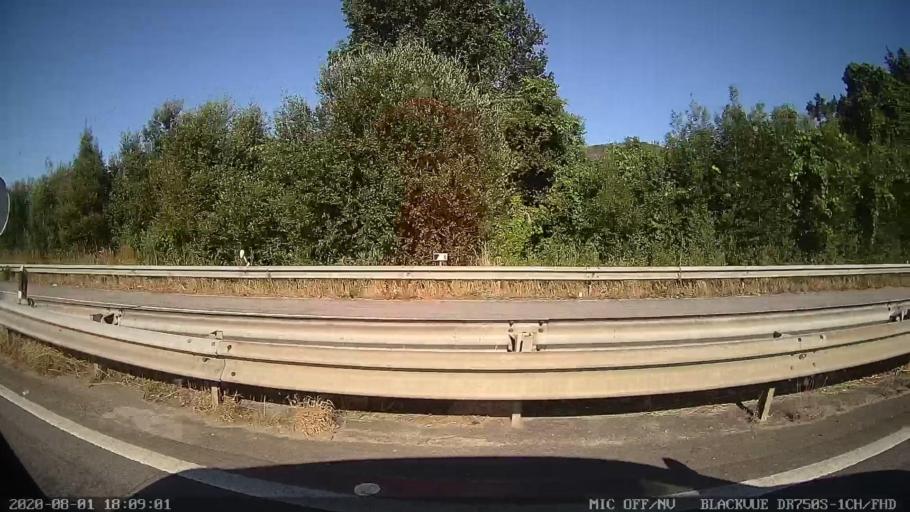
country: PT
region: Porto
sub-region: Santo Tirso
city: Sao Miguel do Couto
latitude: 41.3179
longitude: -8.4694
